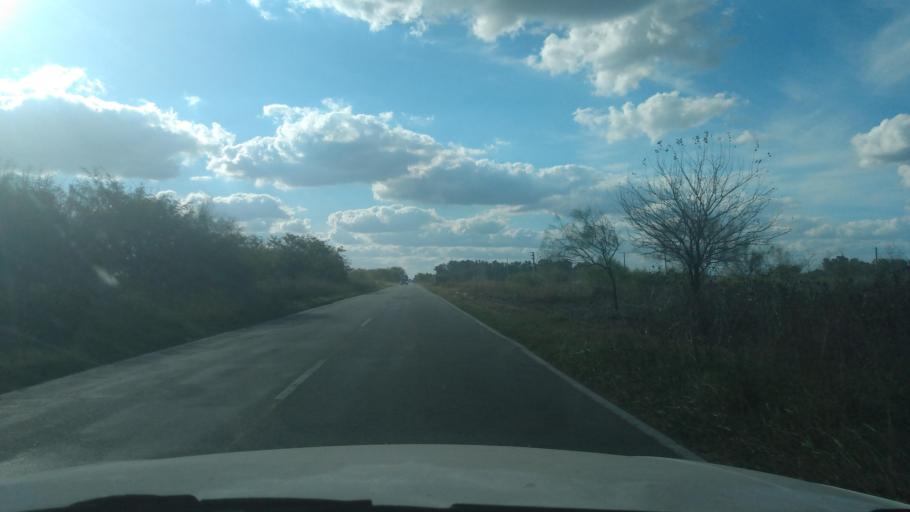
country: AR
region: Buenos Aires
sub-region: Partido de Mercedes
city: Mercedes
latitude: -34.7600
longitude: -59.3761
